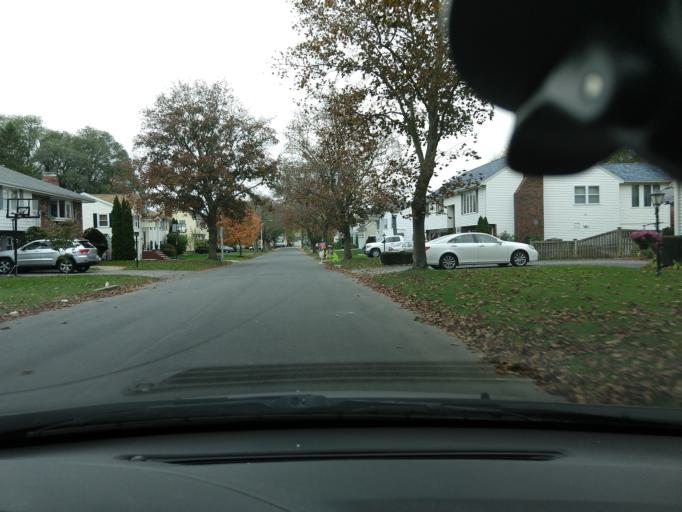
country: US
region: Massachusetts
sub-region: Middlesex County
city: Arlington
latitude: 42.4026
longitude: -71.1623
